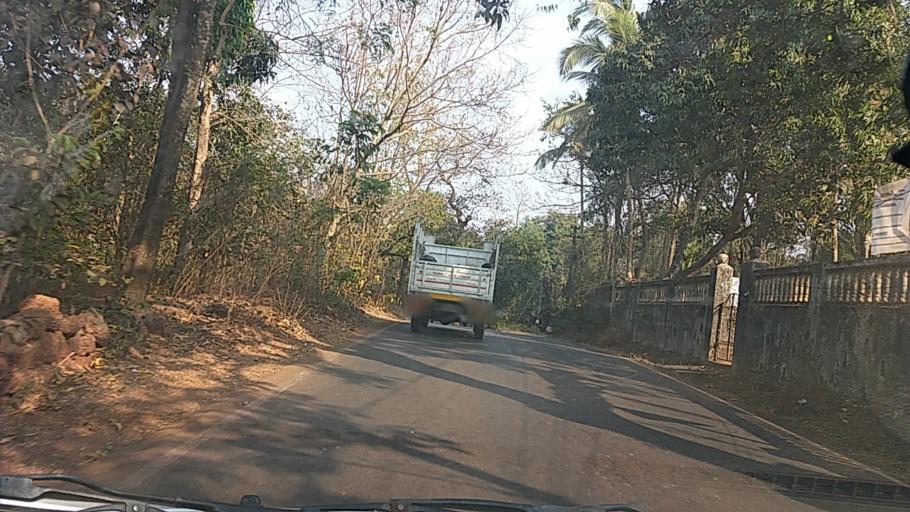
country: IN
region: Goa
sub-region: North Goa
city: Goa Velha
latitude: 15.4792
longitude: 73.9240
